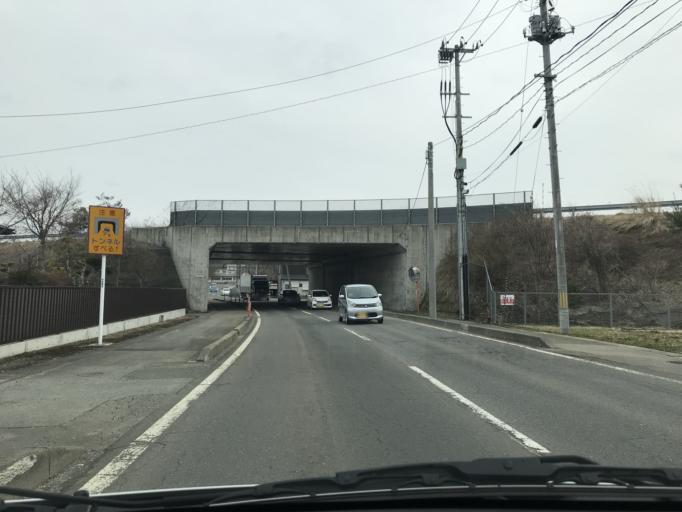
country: JP
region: Iwate
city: Hanamaki
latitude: 39.4175
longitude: 141.1093
